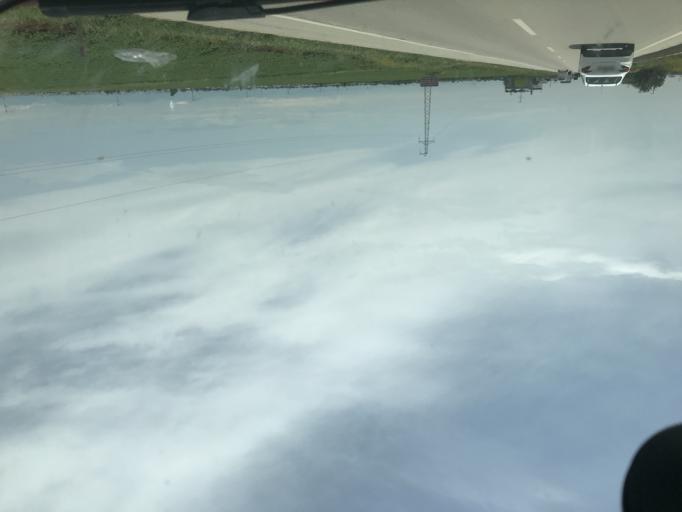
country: TR
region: Adana
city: Yuregir
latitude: 36.9765
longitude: 35.4813
